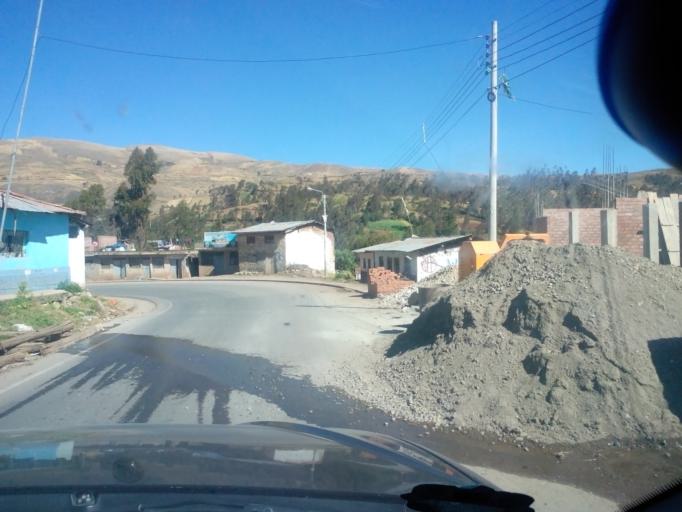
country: PE
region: Apurimac
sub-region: Provincia de Andahuaylas
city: Talavera
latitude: -13.6532
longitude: -73.5292
